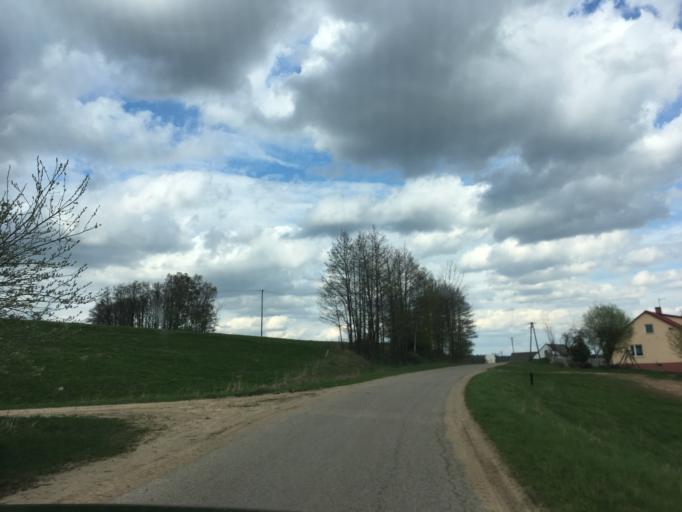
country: PL
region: Podlasie
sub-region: Suwalki
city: Suwalki
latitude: 54.3739
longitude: 22.9367
